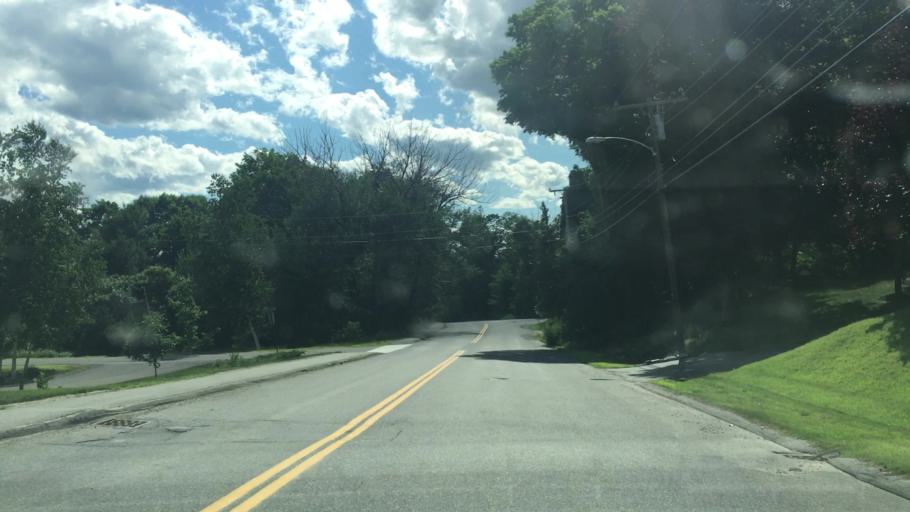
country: US
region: Maine
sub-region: Franklin County
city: Farmington
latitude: 44.6740
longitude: -70.1368
